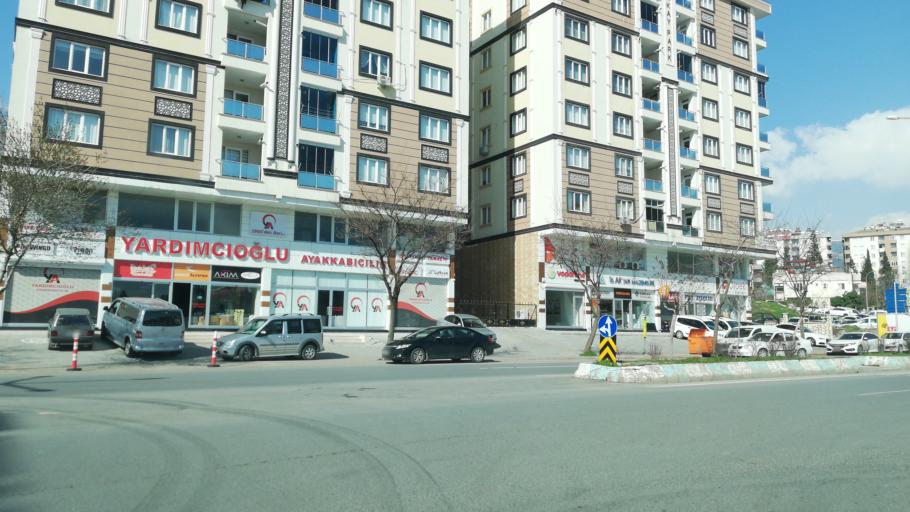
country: TR
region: Kahramanmaras
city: Kahramanmaras
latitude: 37.5736
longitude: 36.9201
